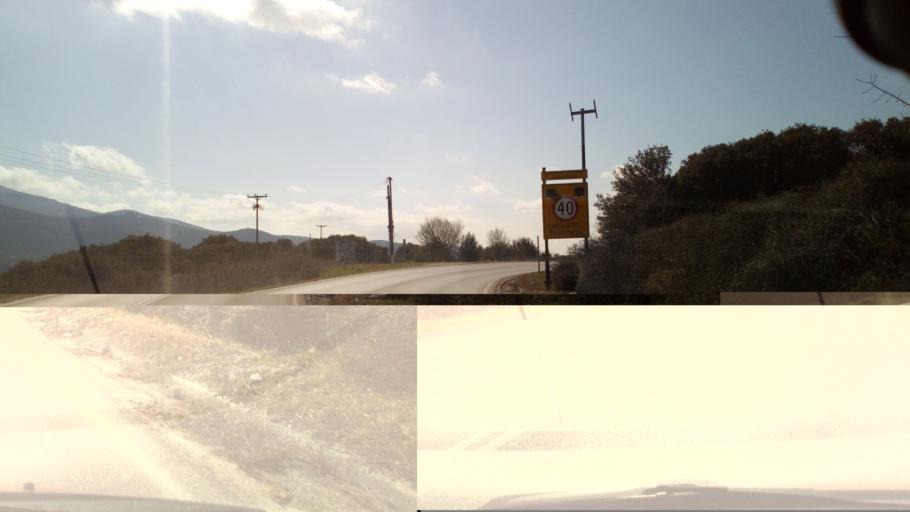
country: GR
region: Central Macedonia
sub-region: Nomos Thessalonikis
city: Chortiatis
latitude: 40.6163
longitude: 23.0611
